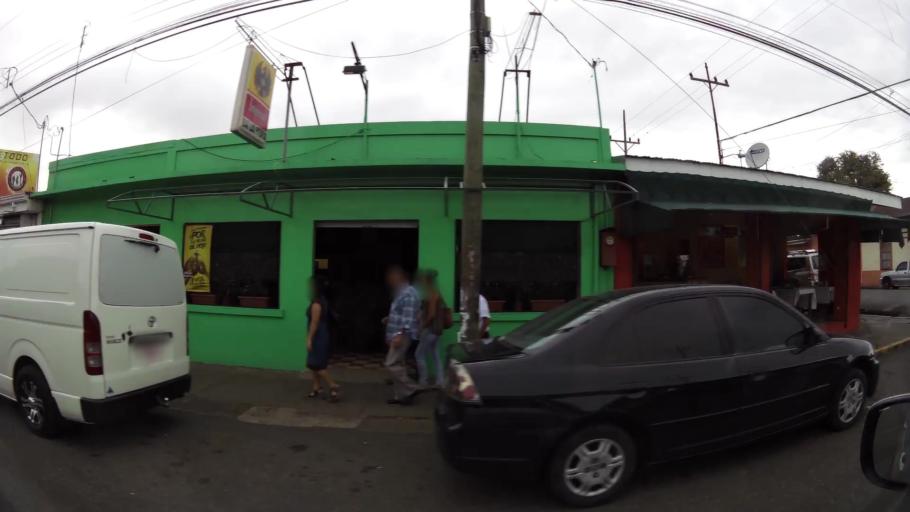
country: CR
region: Alajuela
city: Orotina
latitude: 9.9125
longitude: -84.5249
